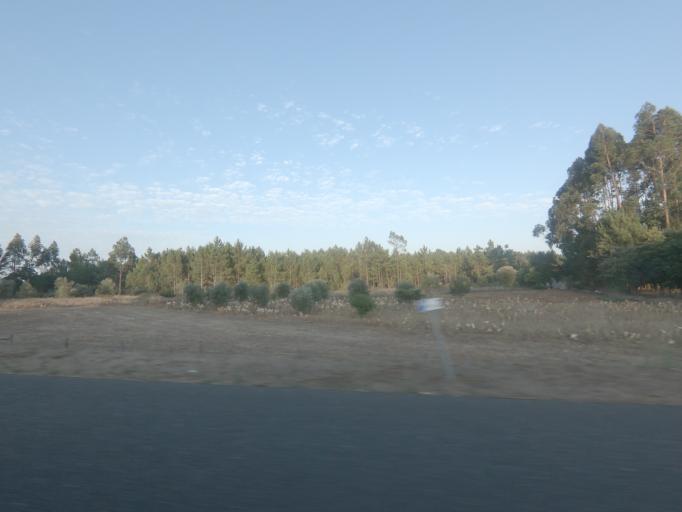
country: PT
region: Leiria
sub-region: Leiria
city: Santa Catarina da Serra
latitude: 39.6485
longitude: -8.6960
